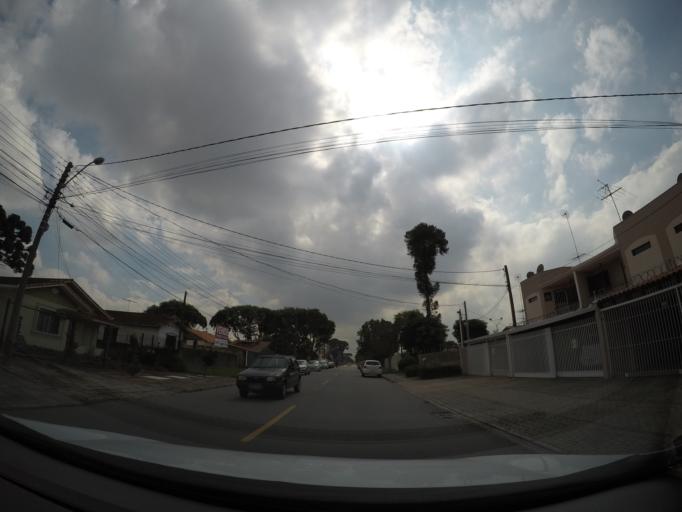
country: BR
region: Parana
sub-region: Sao Jose Dos Pinhais
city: Sao Jose dos Pinhais
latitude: -25.5028
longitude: -49.2395
